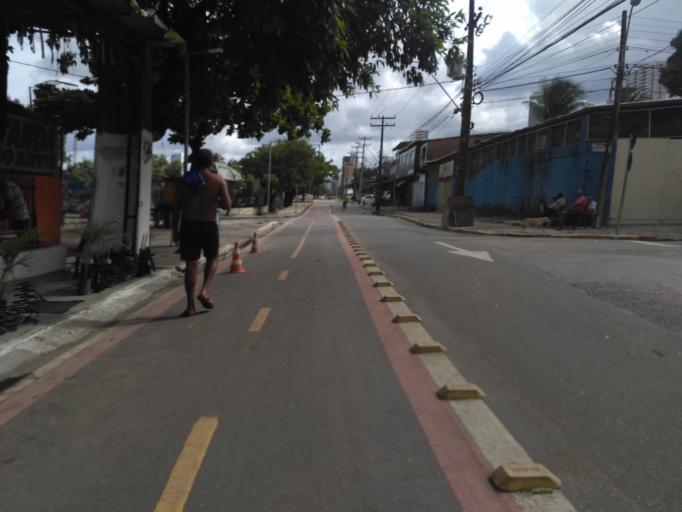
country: BR
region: Pernambuco
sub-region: Recife
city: Recife
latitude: -8.0387
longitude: -34.8778
